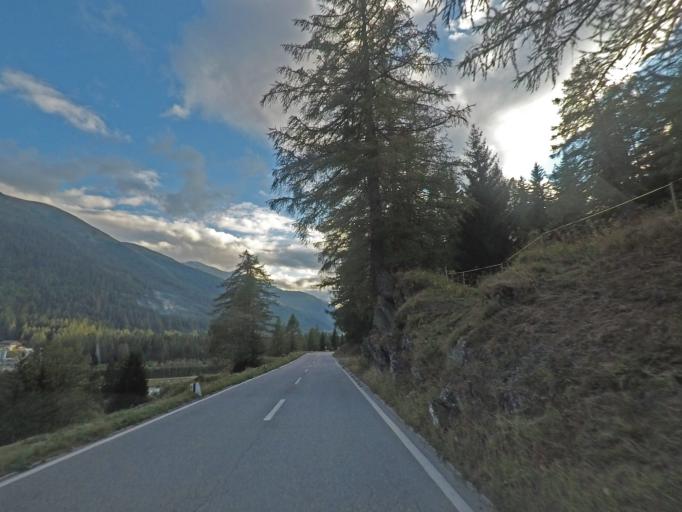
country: IT
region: Piedmont
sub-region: Provincia Verbano-Cusio-Ossola
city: Formazza
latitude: 46.5400
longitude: 8.3574
